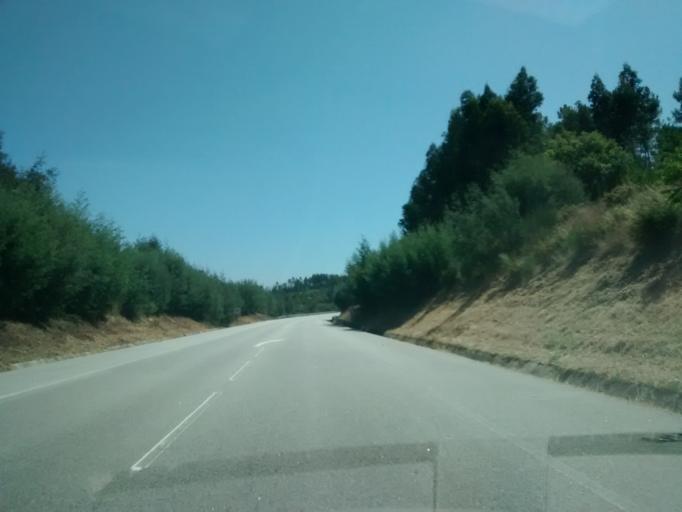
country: PT
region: Coimbra
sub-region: Tabua
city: Tabua
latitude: 40.3729
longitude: -8.0277
